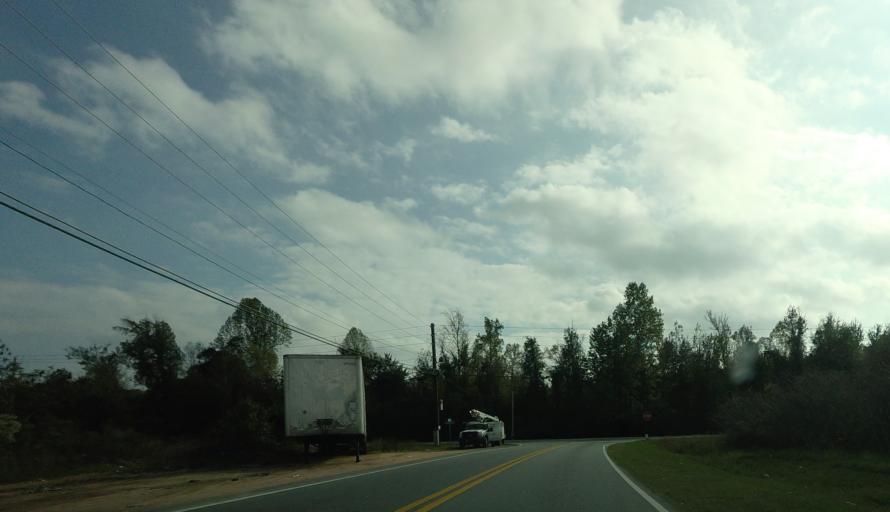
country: US
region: Georgia
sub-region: Bibb County
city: West Point
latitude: 32.8070
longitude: -83.7201
